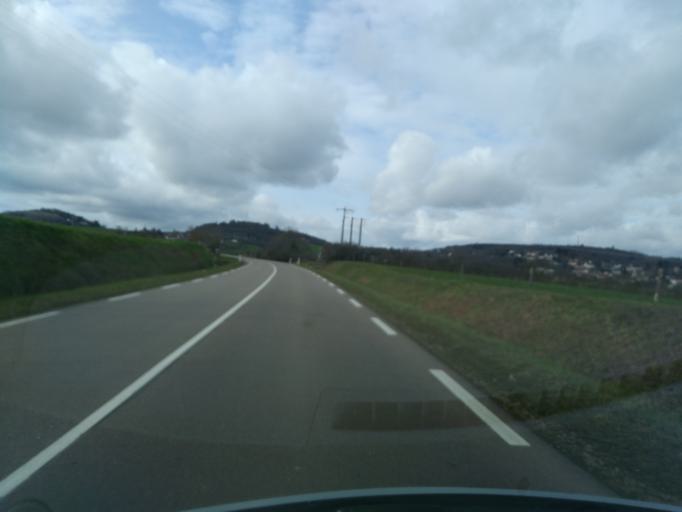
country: FR
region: Bourgogne
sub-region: Departement de Saone-et-Loire
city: Le Creusot
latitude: 46.7823
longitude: 4.4132
